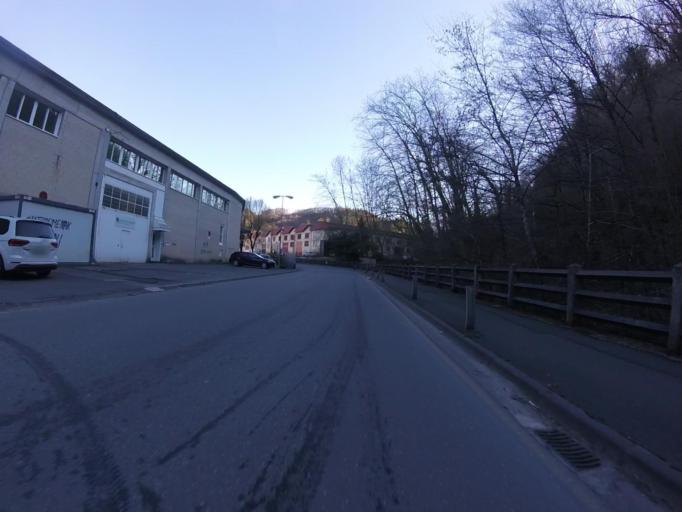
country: ES
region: Basque Country
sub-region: Provincia de Guipuzcoa
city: Errenteria
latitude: 43.2937
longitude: -1.8849
